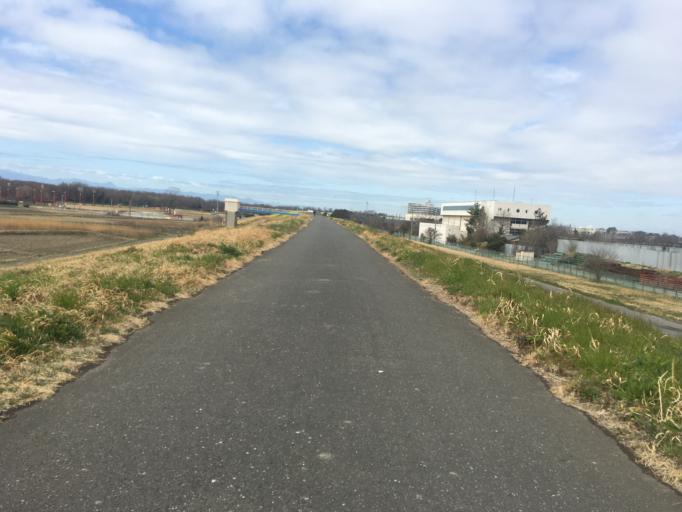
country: JP
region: Saitama
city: Shiki
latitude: 35.8550
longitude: 139.6063
